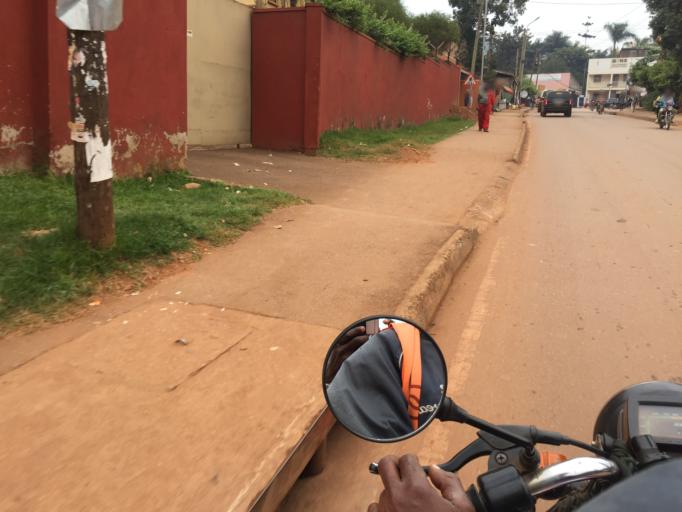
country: UG
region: Central Region
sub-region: Kampala District
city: Kampala
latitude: 0.2862
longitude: 32.6068
